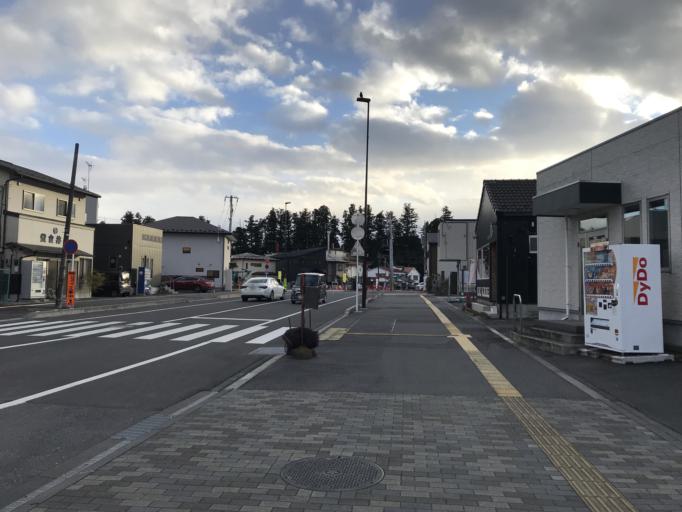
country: JP
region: Tochigi
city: Imaichi
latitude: 36.7253
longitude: 139.6918
